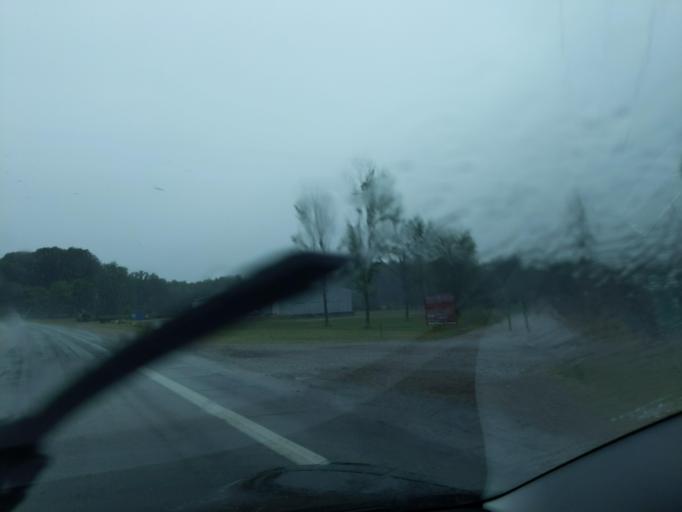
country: US
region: Michigan
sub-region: Muskegon County
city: Fruitport
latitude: 43.1475
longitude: -86.1587
